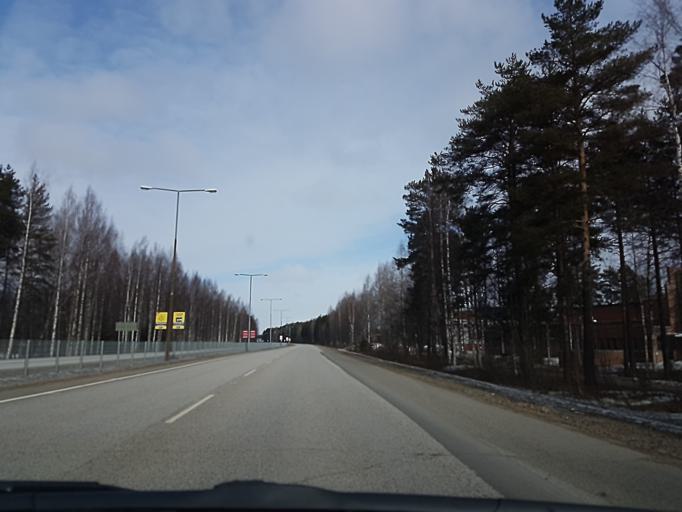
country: FI
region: North Karelia
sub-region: Joensuu
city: Joensuu
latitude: 62.6061
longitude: 29.7452
